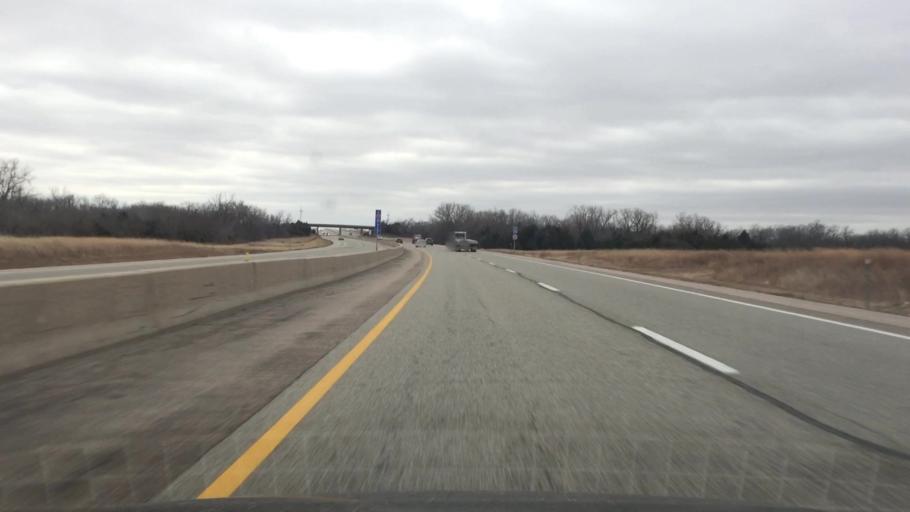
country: US
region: Kansas
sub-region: Butler County
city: El Dorado
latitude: 38.0465
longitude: -96.6404
